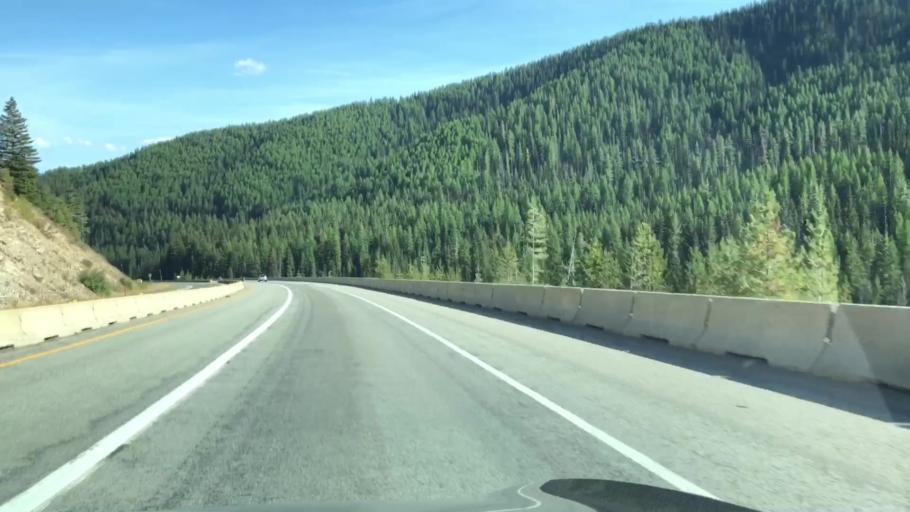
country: US
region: Idaho
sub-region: Shoshone County
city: Wallace
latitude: 47.4379
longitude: -115.6819
